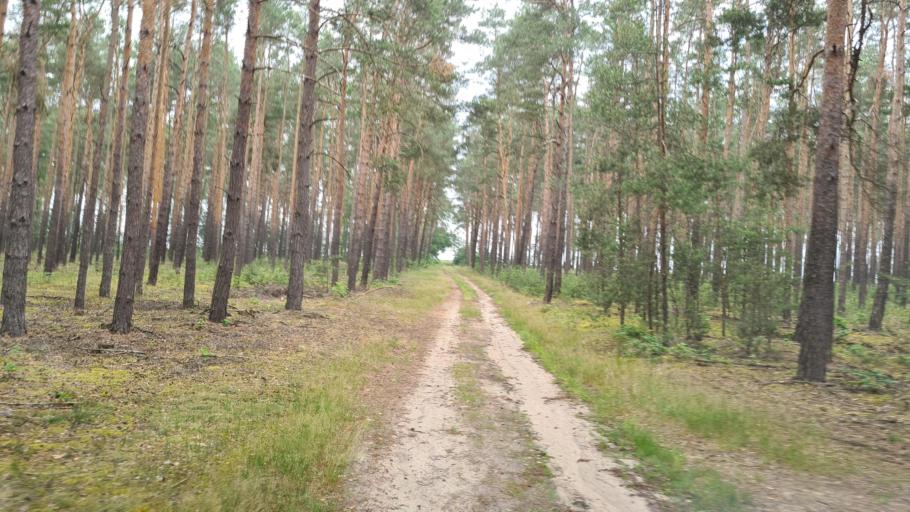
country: DE
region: Brandenburg
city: Crinitz
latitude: 51.7329
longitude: 13.7192
